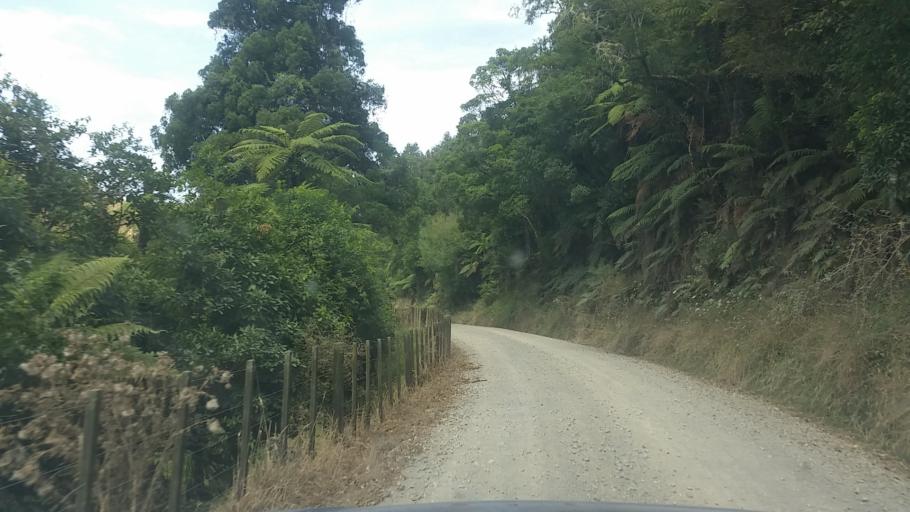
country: NZ
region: Taranaki
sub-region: New Plymouth District
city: Waitara
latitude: -39.0926
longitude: 174.8388
